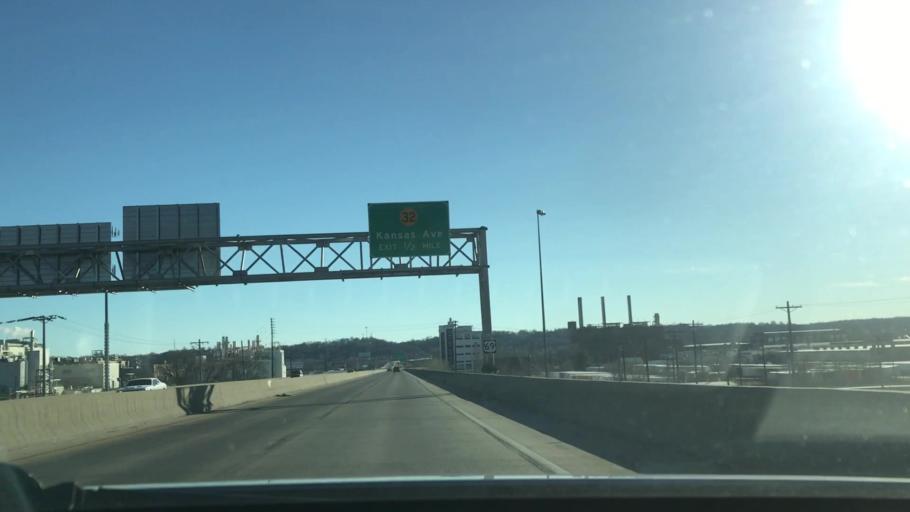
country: US
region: Kansas
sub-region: Wyandotte County
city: Kansas City
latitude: 39.0934
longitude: -94.6495
